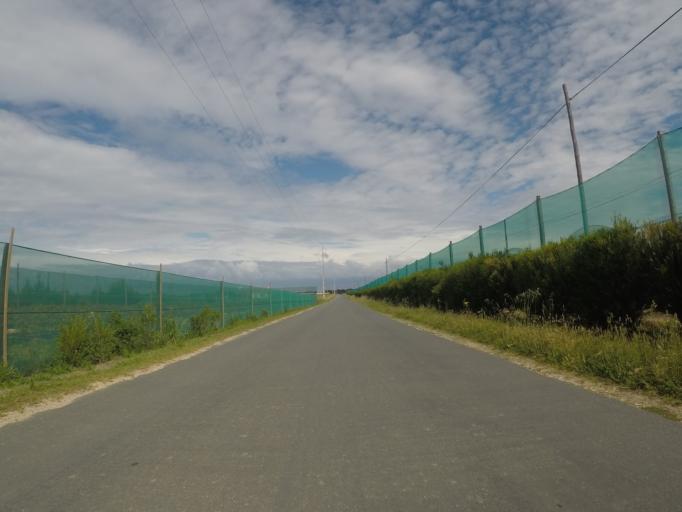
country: PT
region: Beja
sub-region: Odemira
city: Sao Teotonio
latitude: 37.4842
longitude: -8.7706
